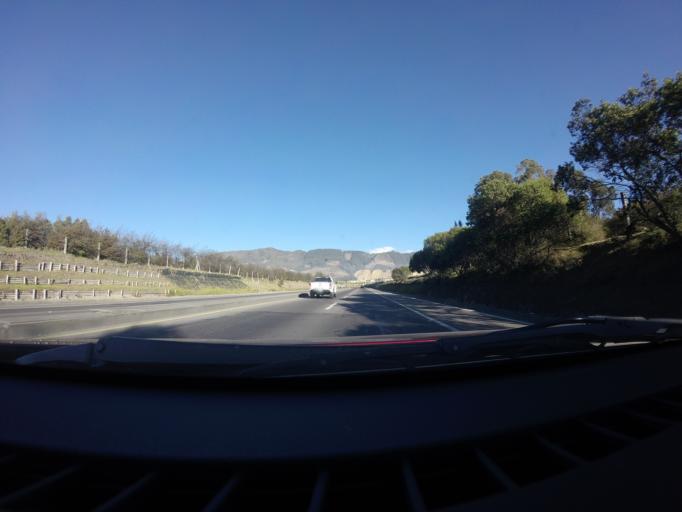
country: CO
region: Cundinamarca
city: Cajica
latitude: 4.9351
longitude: -74.0110
